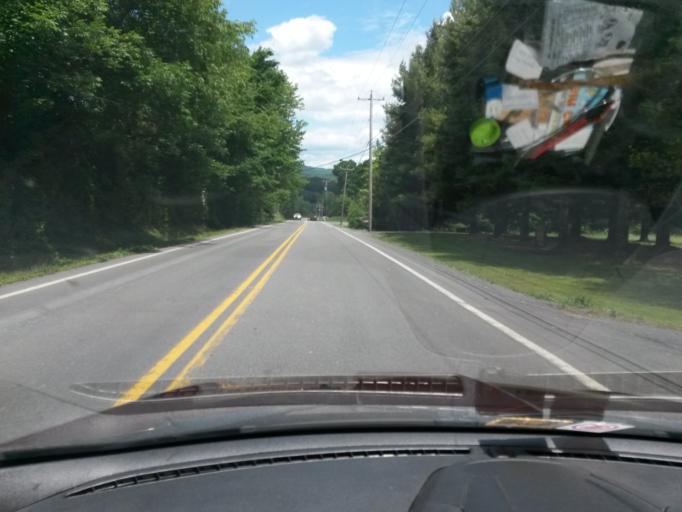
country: US
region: West Virginia
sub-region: Greenbrier County
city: Rainelle
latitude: 37.9529
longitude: -80.6675
